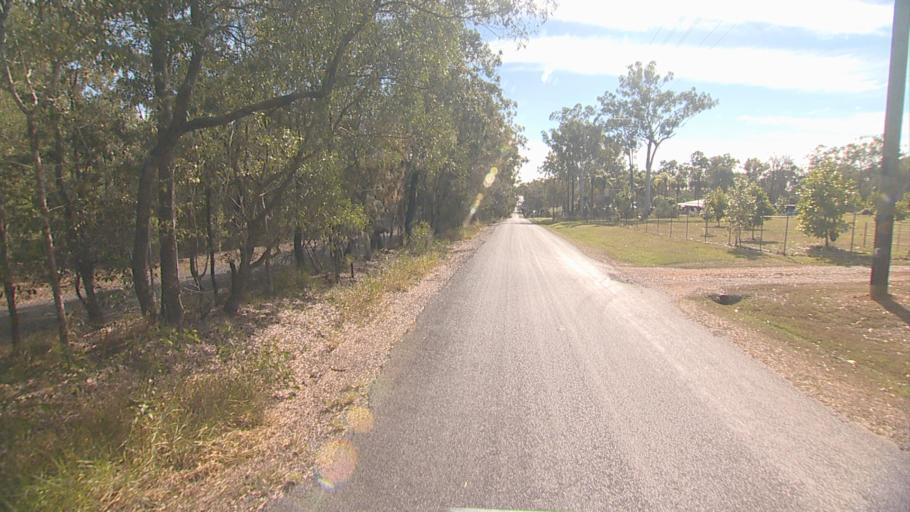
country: AU
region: Queensland
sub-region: Brisbane
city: Forest Lake
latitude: -27.6532
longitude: 152.9833
